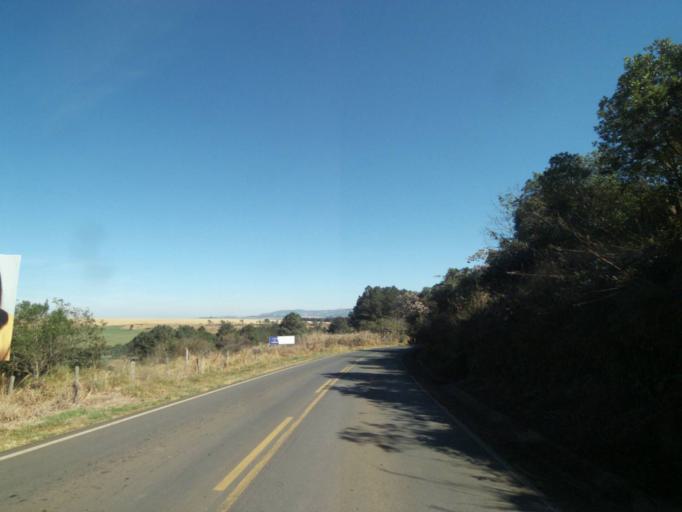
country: BR
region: Parana
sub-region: Tibagi
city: Tibagi
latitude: -24.5277
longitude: -50.3855
